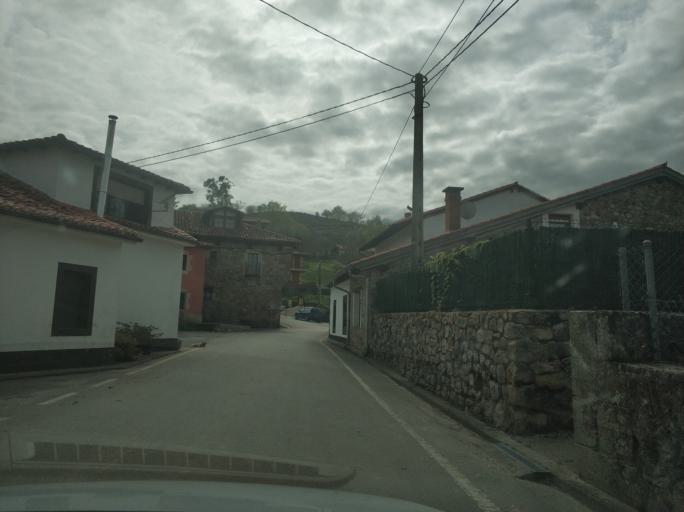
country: ES
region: Cantabria
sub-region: Provincia de Cantabria
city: Ruente
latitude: 43.2338
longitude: -4.2815
